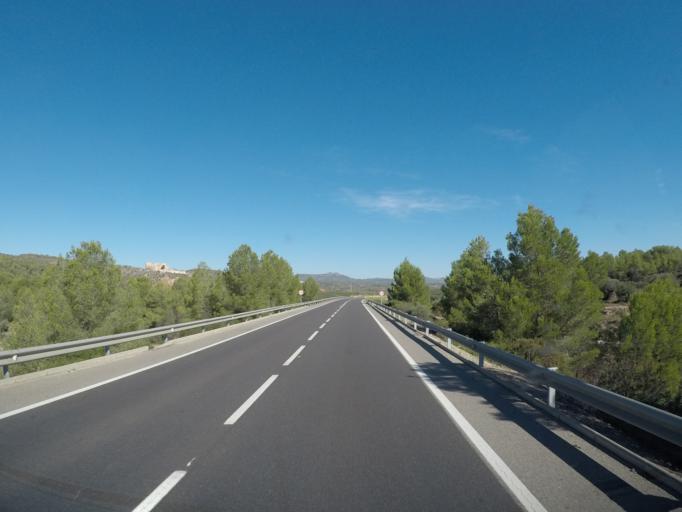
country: ES
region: Catalonia
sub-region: Provincia de Tarragona
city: Miravet
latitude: 41.0256
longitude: 0.6043
